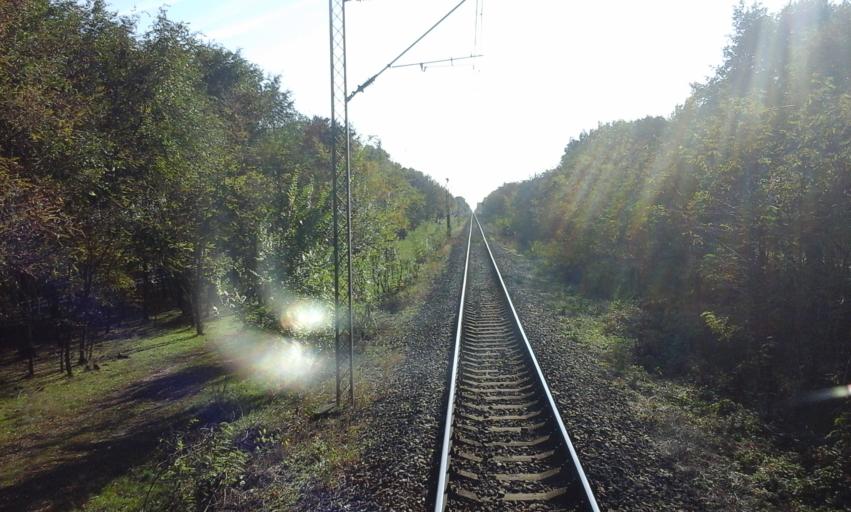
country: RS
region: Autonomna Pokrajina Vojvodina
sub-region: Severnobacki Okrug
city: Backa Topola
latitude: 45.8556
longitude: 19.6553
